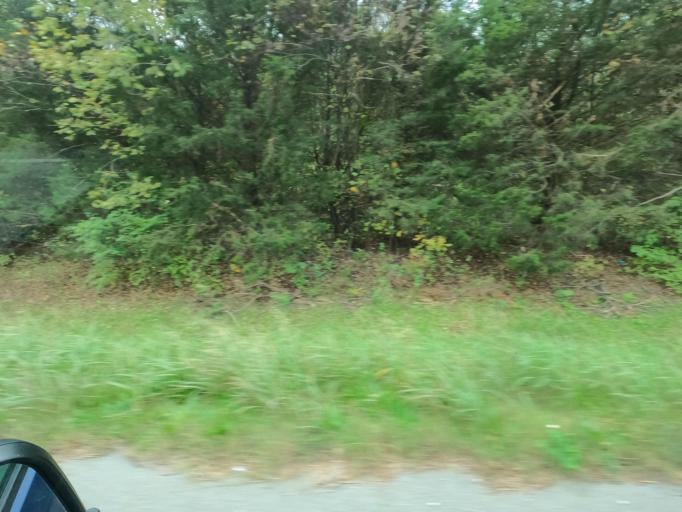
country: US
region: Tennessee
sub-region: Cheatham County
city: Pegram
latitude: 36.0943
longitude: -87.0410
